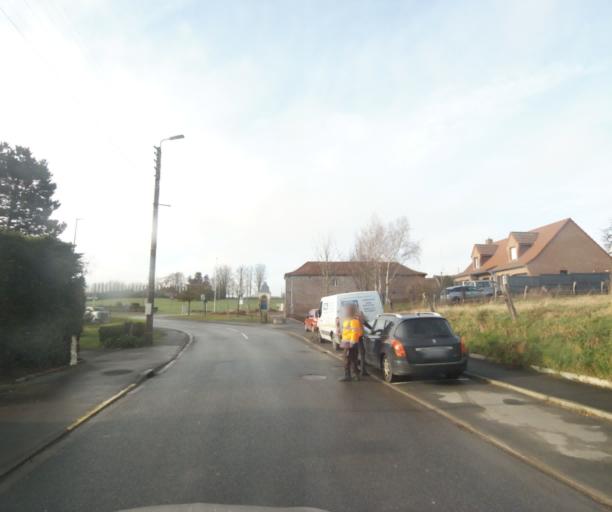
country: FR
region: Nord-Pas-de-Calais
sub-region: Departement du Nord
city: Thiant
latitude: 50.2857
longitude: 3.4501
